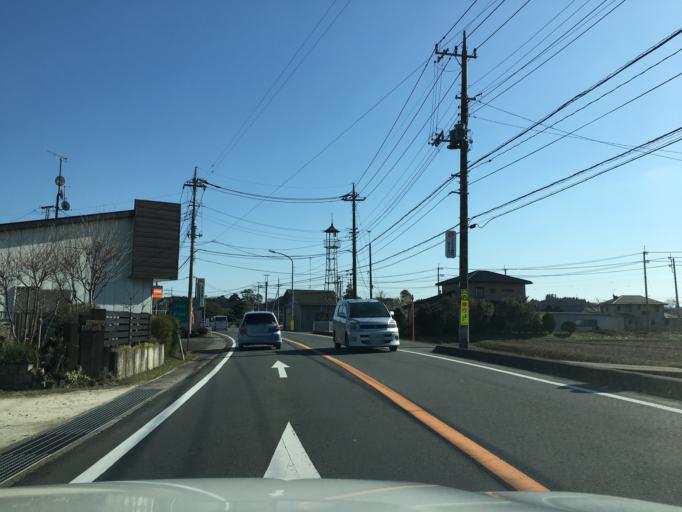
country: JP
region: Ibaraki
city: Omiya
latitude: 36.4973
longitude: 140.3719
